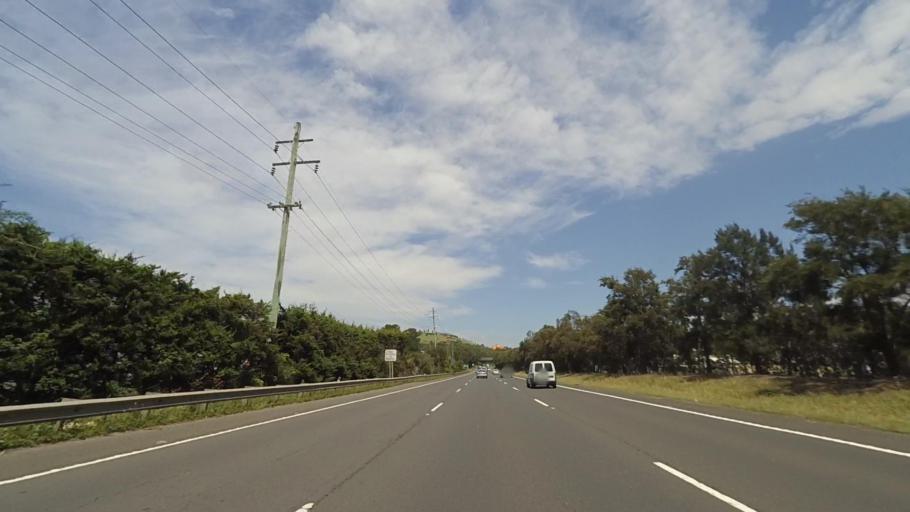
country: AU
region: New South Wales
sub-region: Wollongong
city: Mount Saint Thomas
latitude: -34.4585
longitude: 150.8552
